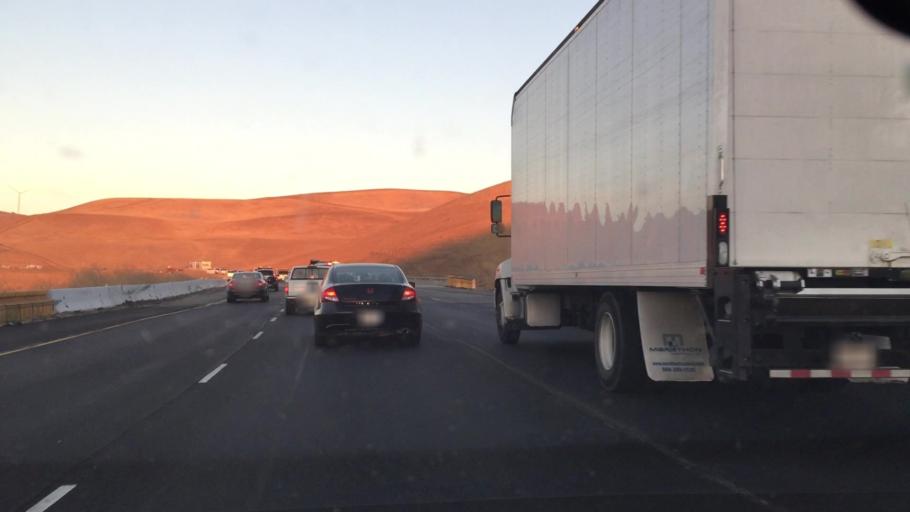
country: US
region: California
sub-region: San Joaquin County
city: Mountain House
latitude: 37.7343
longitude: -121.6293
